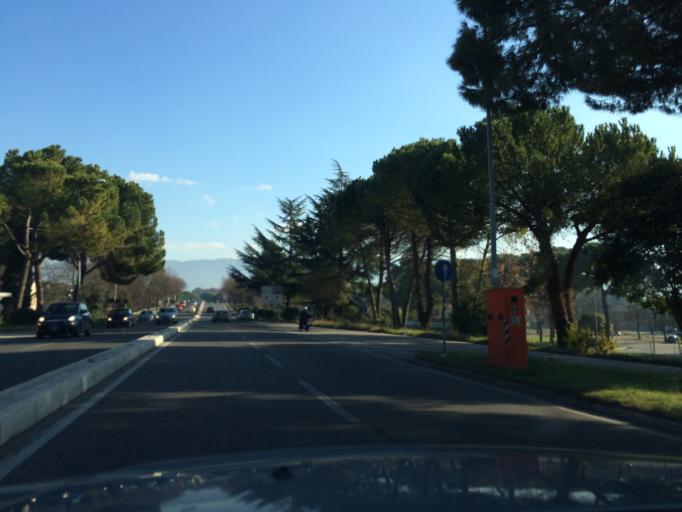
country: IT
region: Umbria
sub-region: Provincia di Terni
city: Terni
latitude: 42.5668
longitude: 12.6342
